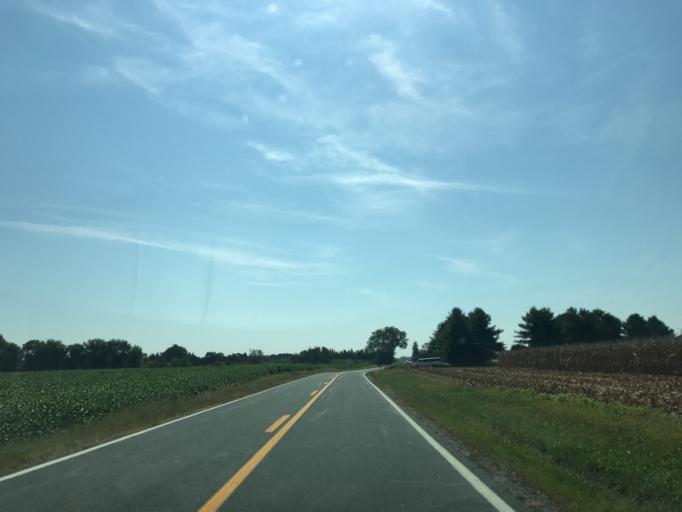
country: US
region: Maryland
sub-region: Queen Anne's County
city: Kingstown
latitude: 39.3386
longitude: -75.9546
